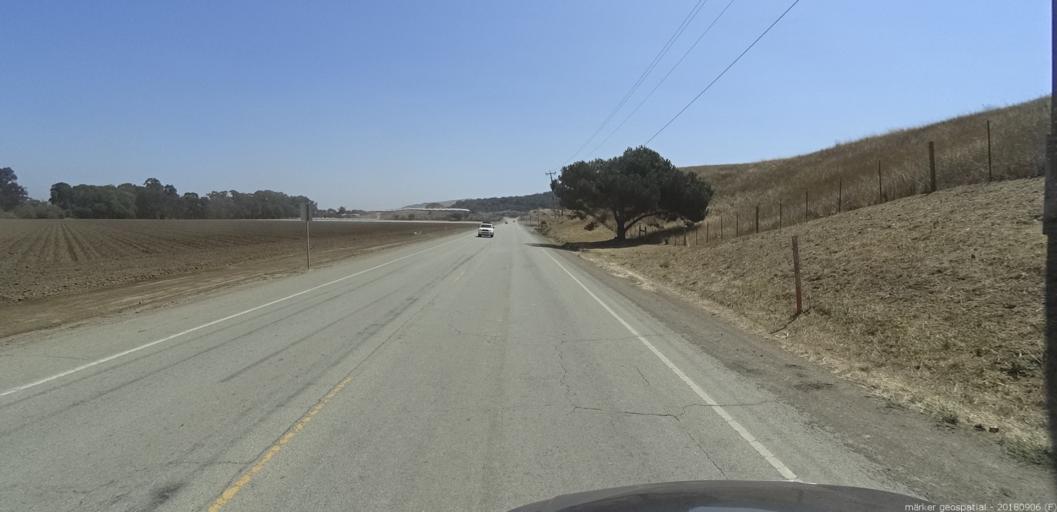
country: US
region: California
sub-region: Monterey County
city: Salinas
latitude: 36.6382
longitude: -121.7031
